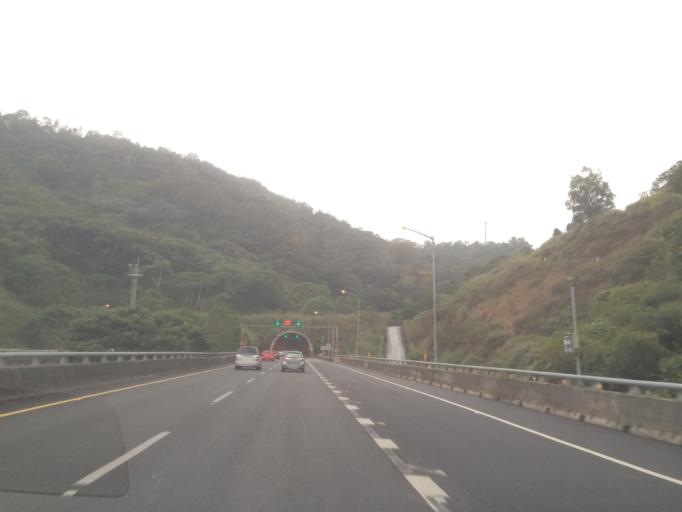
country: TW
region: Taiwan
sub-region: Nantou
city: Puli
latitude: 23.9791
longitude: 120.8812
